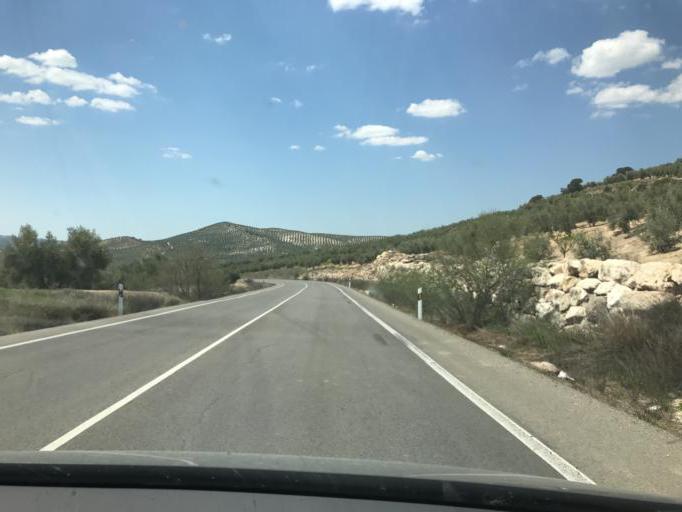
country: ES
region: Andalusia
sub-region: Provincia de Jaen
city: Frailes
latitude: 37.4424
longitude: -3.8288
